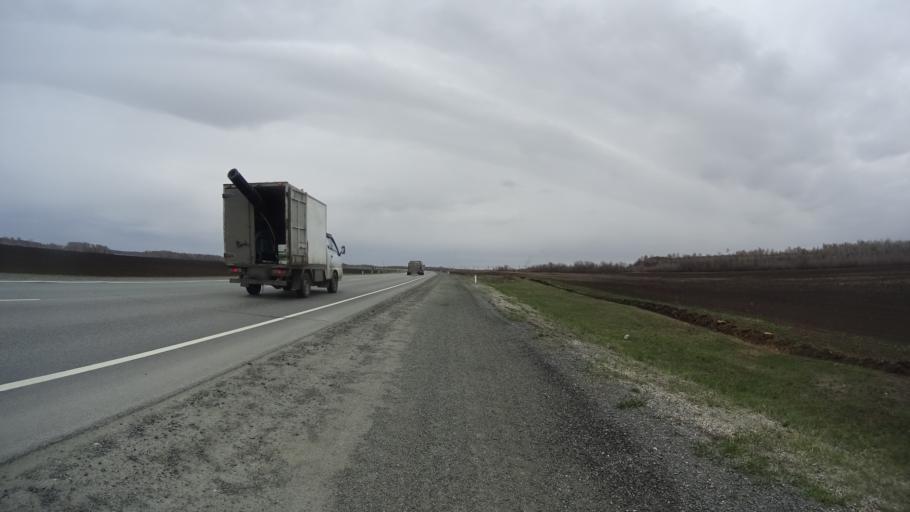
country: RU
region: Chelyabinsk
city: Krasnogorskiy
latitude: 54.5696
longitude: 61.2903
